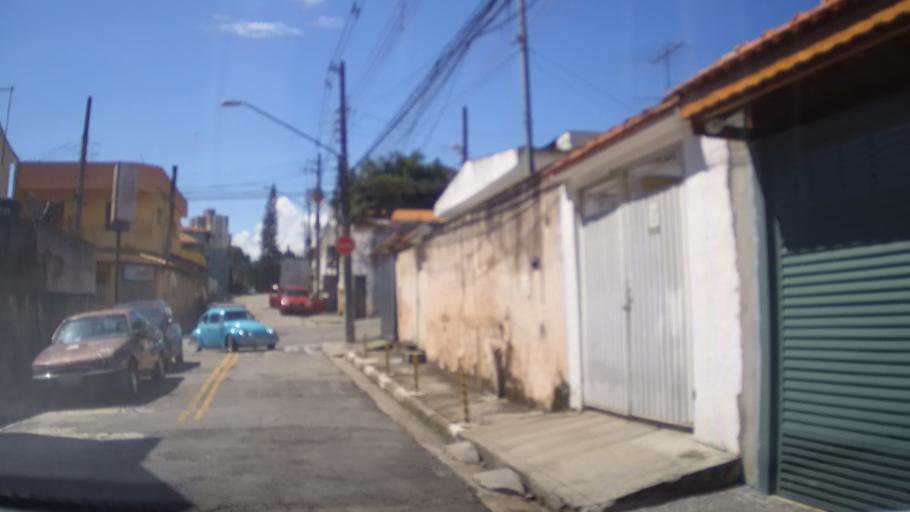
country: BR
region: Sao Paulo
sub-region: Guarulhos
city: Guarulhos
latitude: -23.4570
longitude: -46.5407
